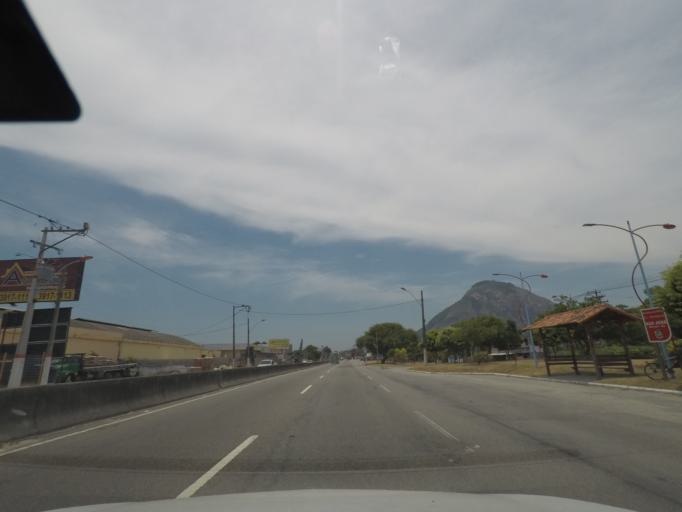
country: BR
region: Rio de Janeiro
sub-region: Marica
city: Marica
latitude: -22.9324
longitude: -42.8873
